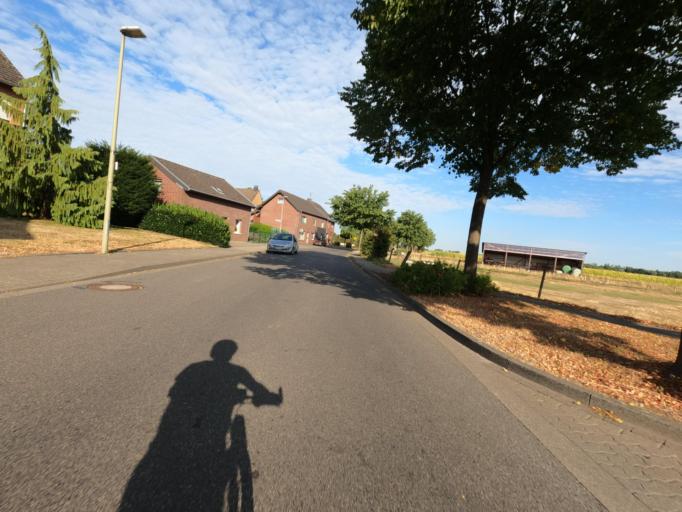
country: DE
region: North Rhine-Westphalia
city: Wegberg
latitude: 51.1114
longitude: 6.2590
